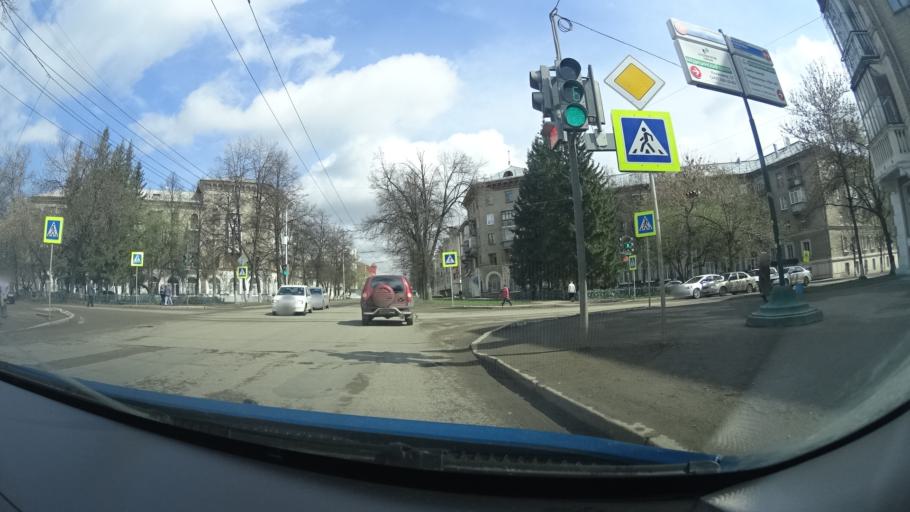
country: RU
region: Bashkortostan
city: Ufa
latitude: 54.8199
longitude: 56.0769
